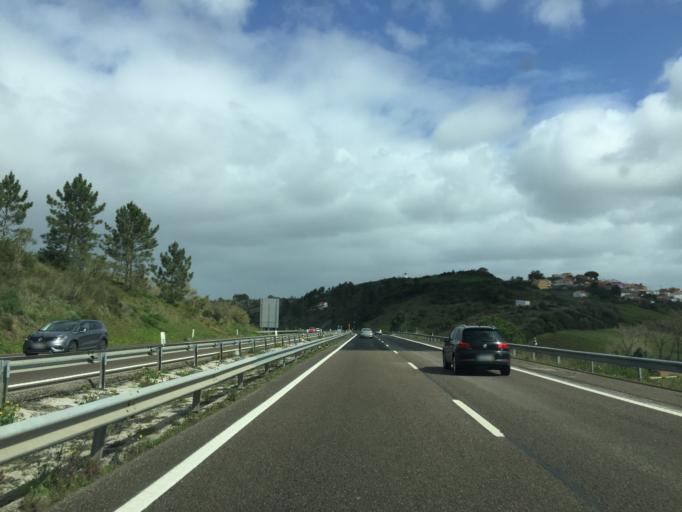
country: PT
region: Lisbon
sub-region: Torres Vedras
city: Torres Vedras
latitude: 39.0699
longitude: -9.2312
